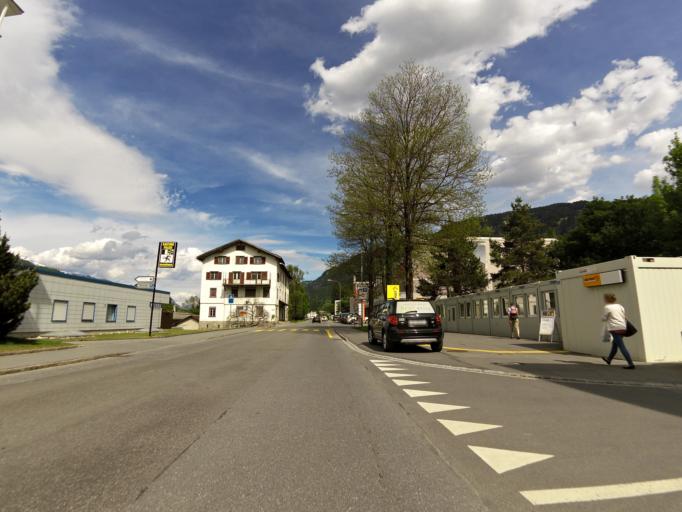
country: CH
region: Grisons
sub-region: Surselva District
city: Ilanz
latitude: 46.7743
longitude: 9.2085
